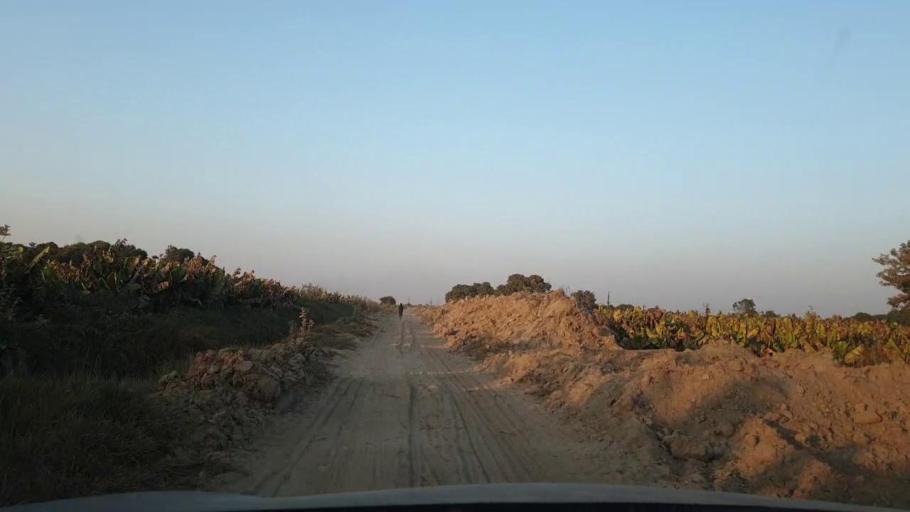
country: PK
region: Sindh
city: Tando Allahyar
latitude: 25.5288
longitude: 68.7359
